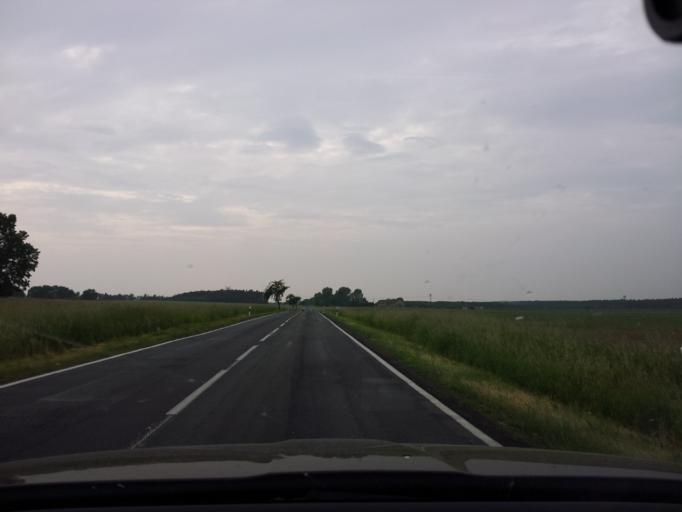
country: DE
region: Brandenburg
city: Treuenbrietzen
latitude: 52.0961
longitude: 12.8554
